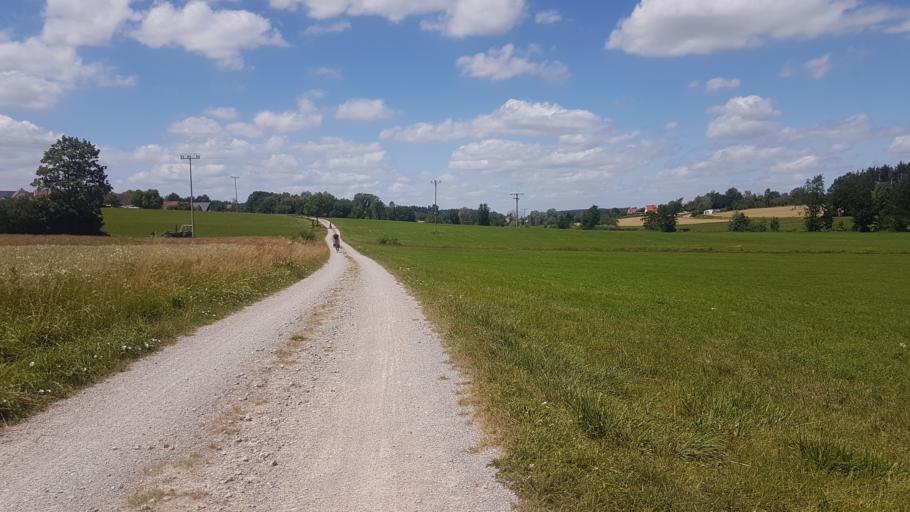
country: DE
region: Bavaria
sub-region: Regierungsbezirk Mittelfranken
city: Leutershausen
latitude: 49.3195
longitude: 10.3851
